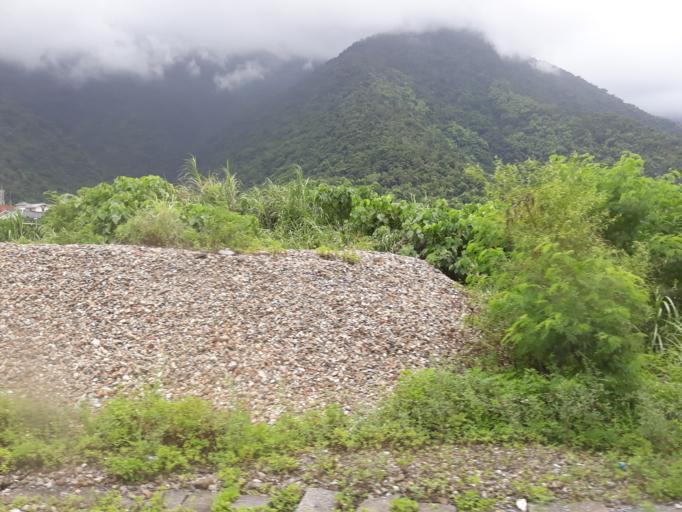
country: TW
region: Taiwan
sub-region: Yilan
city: Yilan
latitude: 24.4626
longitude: 121.8040
